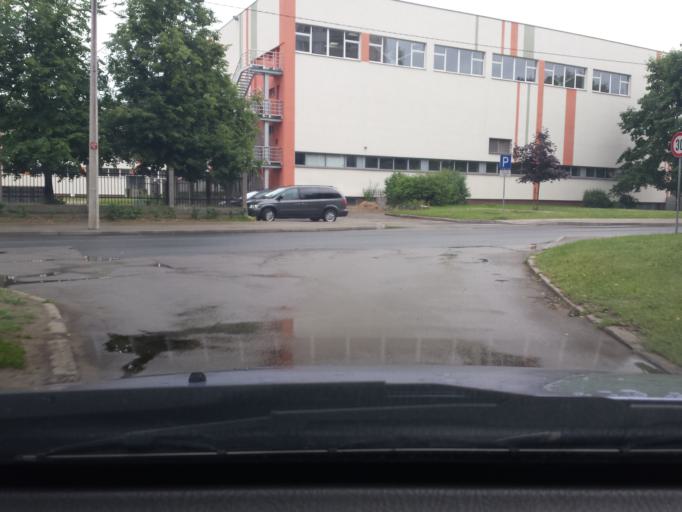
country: LV
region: Kekava
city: Kekava
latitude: 56.9024
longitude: 24.2068
